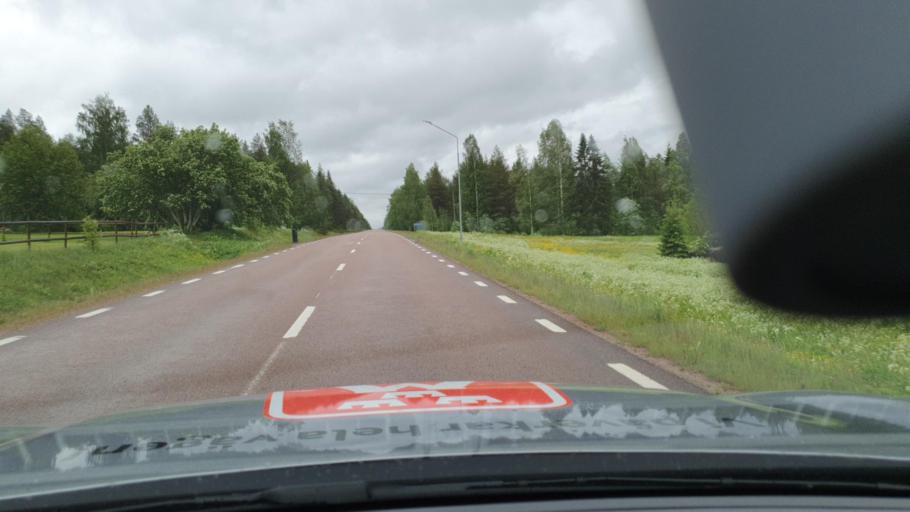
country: FI
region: Lapland
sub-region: Torniolaakso
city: Ylitornio
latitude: 66.1618
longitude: 23.8583
